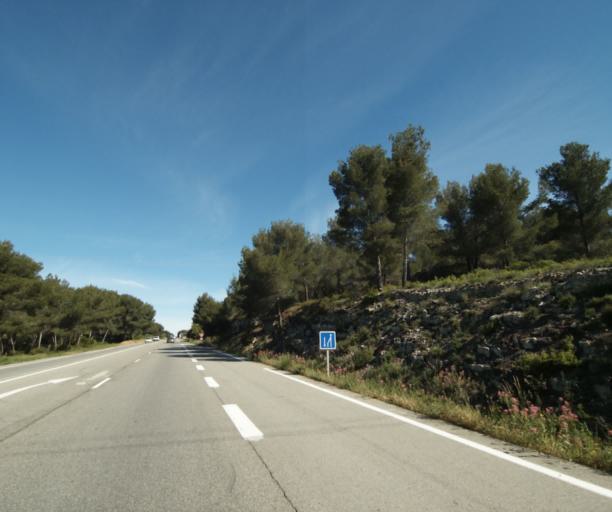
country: FR
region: Provence-Alpes-Cote d'Azur
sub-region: Departement des Bouches-du-Rhone
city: Rognac
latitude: 43.5047
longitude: 5.2094
